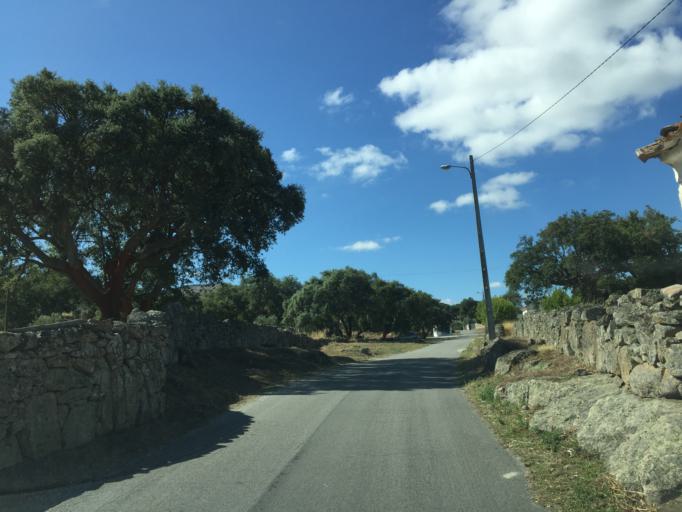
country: PT
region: Portalegre
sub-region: Marvao
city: Marvao
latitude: 39.4202
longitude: -7.3610
